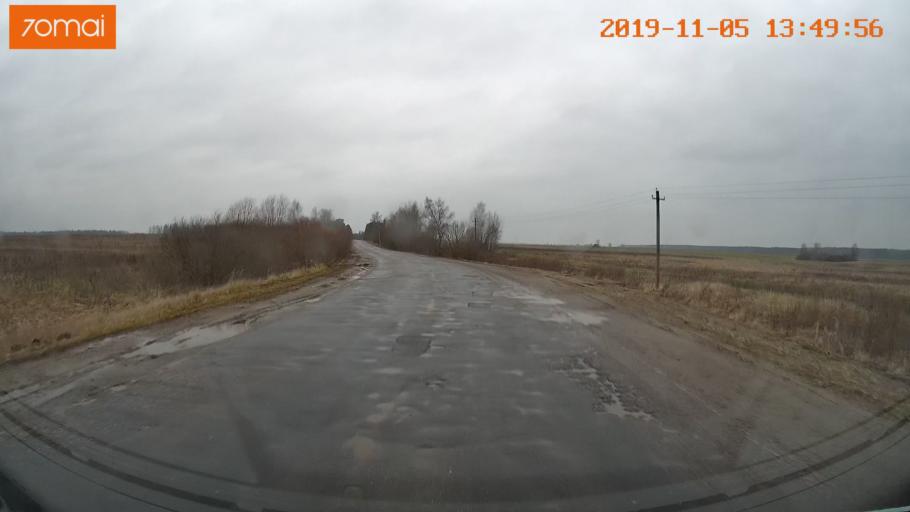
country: RU
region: Ivanovo
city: Kaminskiy
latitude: 57.0154
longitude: 41.4106
